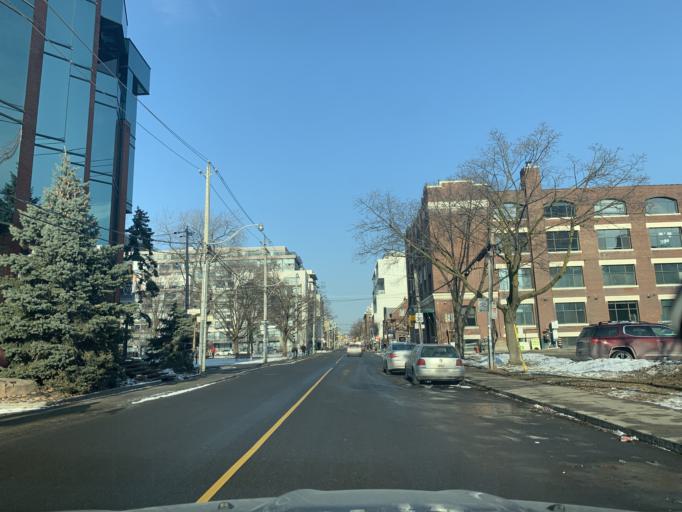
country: CA
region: Ontario
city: Toronto
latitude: 43.6421
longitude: -79.3991
